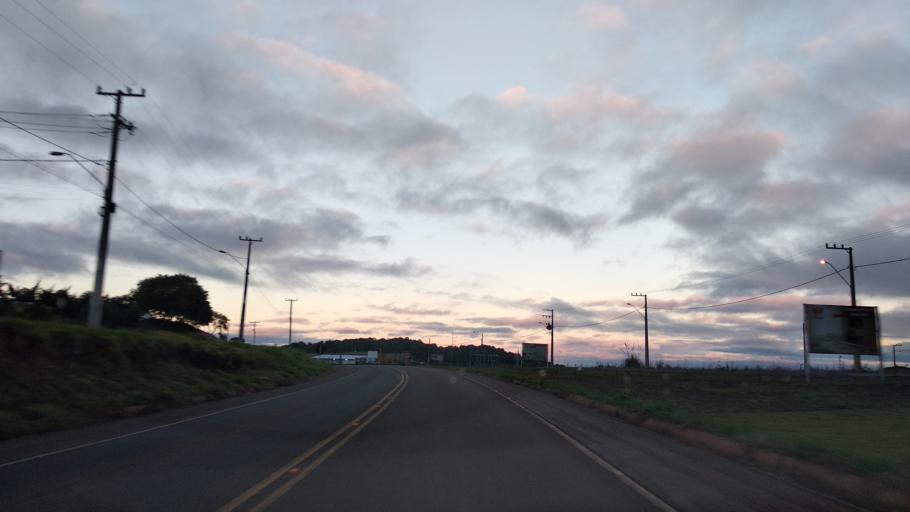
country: BR
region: Santa Catarina
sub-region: Campos Novos
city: Campos Novos
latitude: -27.3777
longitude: -51.2071
